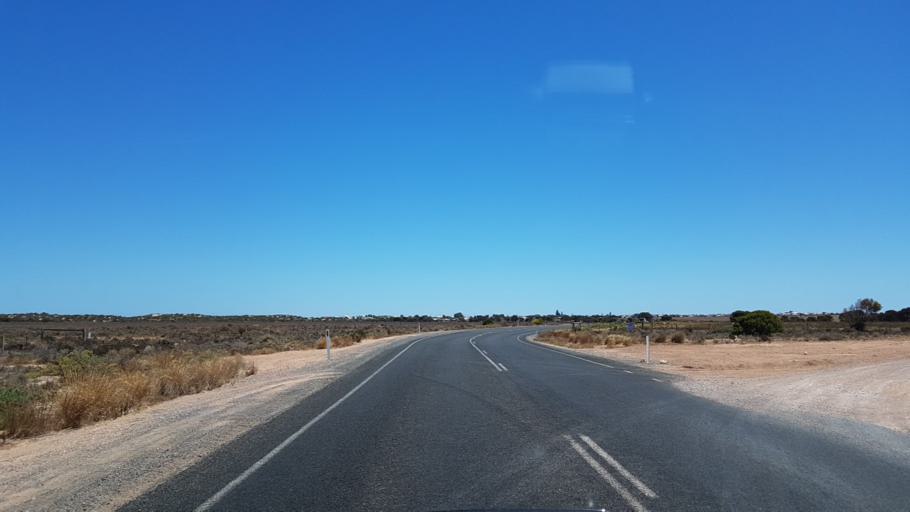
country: AU
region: South Australia
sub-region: Copper Coast
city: Wallaroo
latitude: -33.9132
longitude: 137.6447
